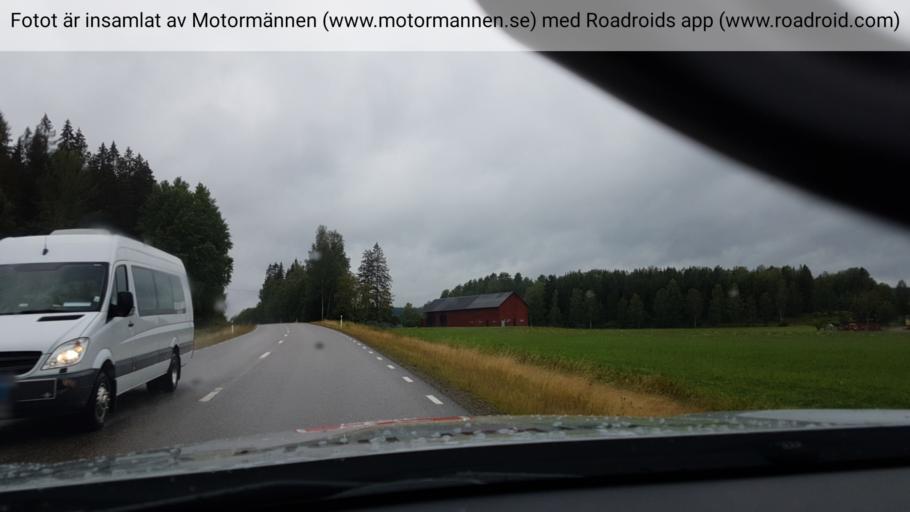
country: SE
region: Vaestra Goetaland
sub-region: Bengtsfors Kommun
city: Billingsfors
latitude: 58.9475
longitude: 12.2162
